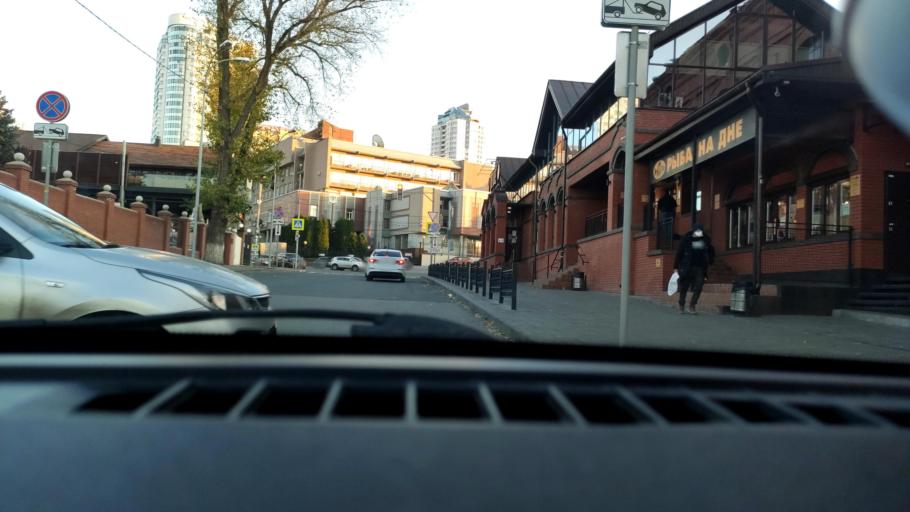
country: RU
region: Samara
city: Samara
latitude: 53.2017
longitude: 50.0993
